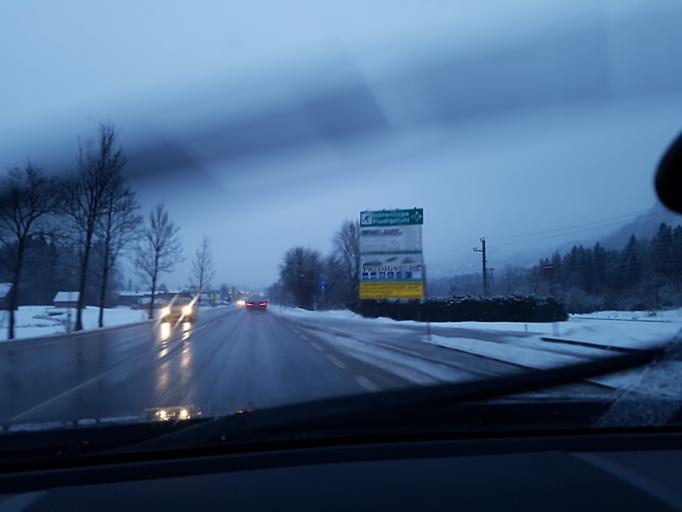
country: AT
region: Upper Austria
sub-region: Politischer Bezirk Gmunden
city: Bad Goisern
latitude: 47.6585
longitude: 13.6094
